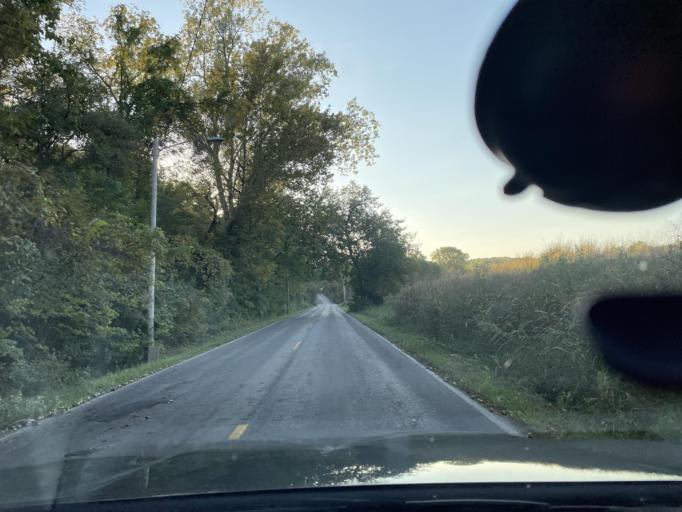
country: US
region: Missouri
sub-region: Buchanan County
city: Saint Joseph
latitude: 39.7993
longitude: -94.8350
